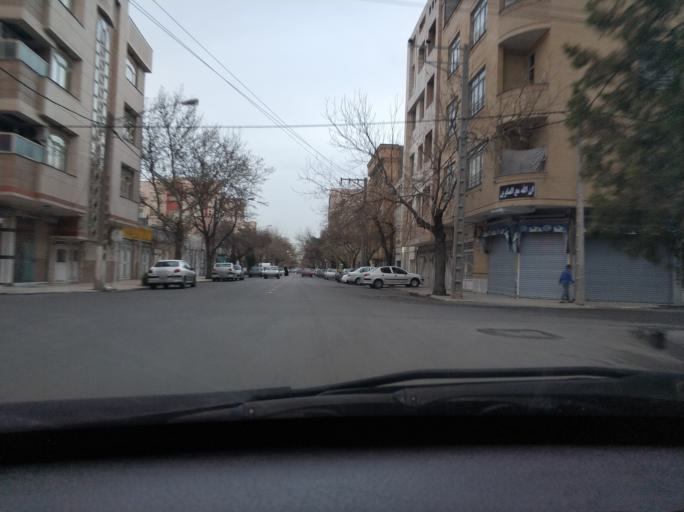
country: IR
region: Razavi Khorasan
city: Mashhad
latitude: 36.2737
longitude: 59.5970
